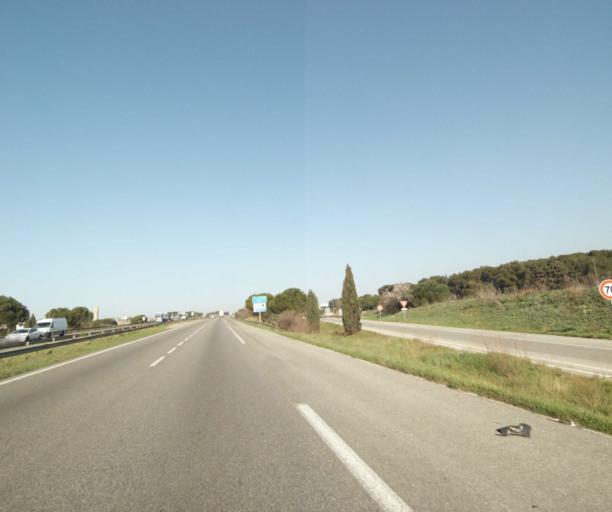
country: FR
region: Provence-Alpes-Cote d'Azur
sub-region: Departement des Bouches-du-Rhone
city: Vitrolles
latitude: 43.4421
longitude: 5.2471
